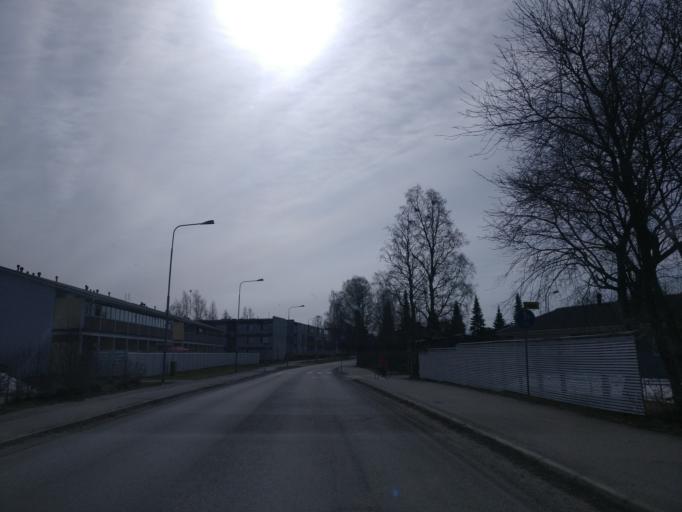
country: FI
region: Lapland
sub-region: Kemi-Tornio
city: Kemi
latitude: 65.7496
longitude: 24.5611
